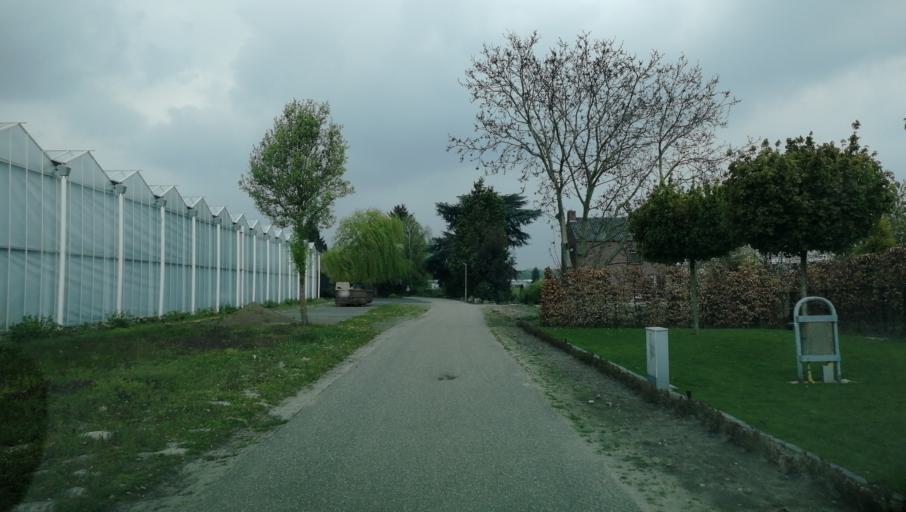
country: NL
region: Limburg
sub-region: Gemeente Venlo
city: Venlo
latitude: 51.3902
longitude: 6.2058
